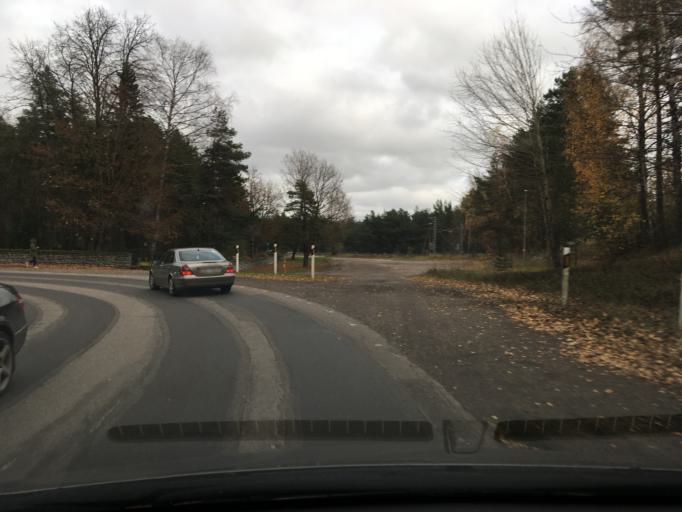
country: EE
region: Harju
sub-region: Tallinna linn
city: Tallinn
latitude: 59.3907
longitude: 24.7082
